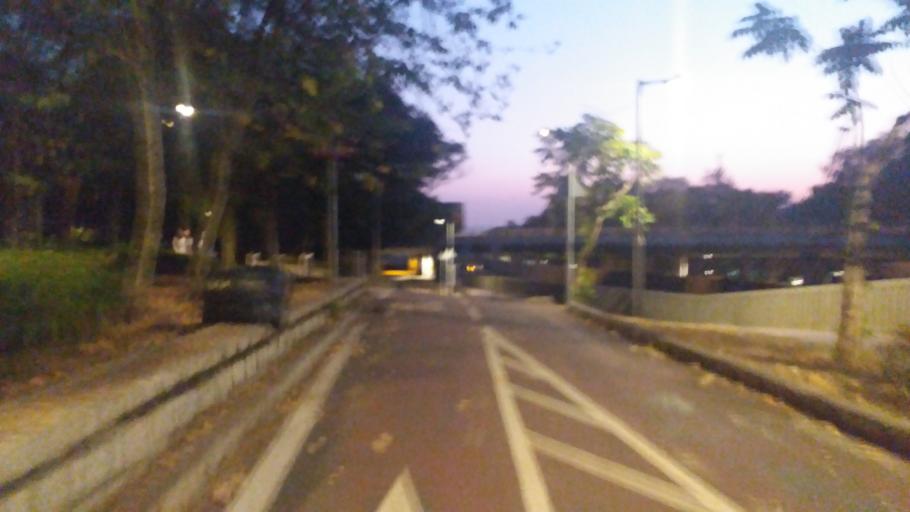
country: HK
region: Yuen Long
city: Yuen Long Kau Hui
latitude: 22.4504
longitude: 113.9991
